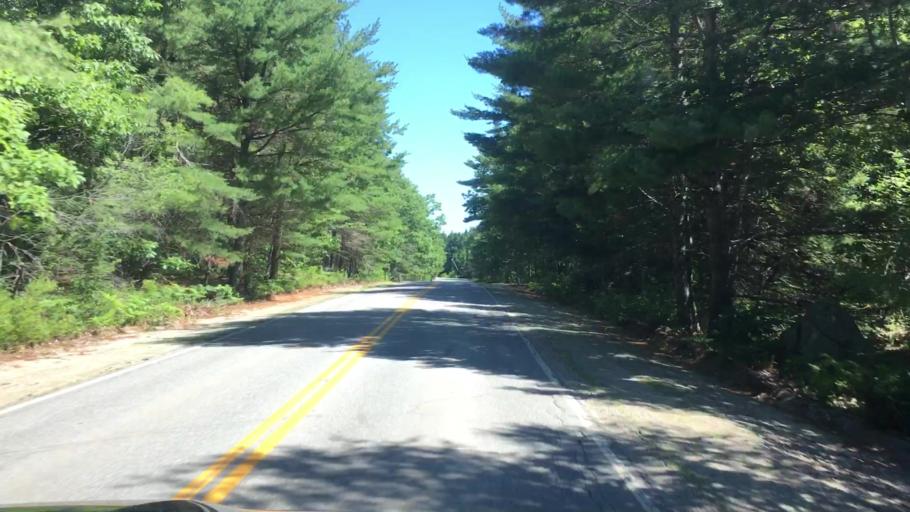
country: US
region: Maine
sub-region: Hancock County
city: Penobscot
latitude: 44.4432
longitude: -68.7046
